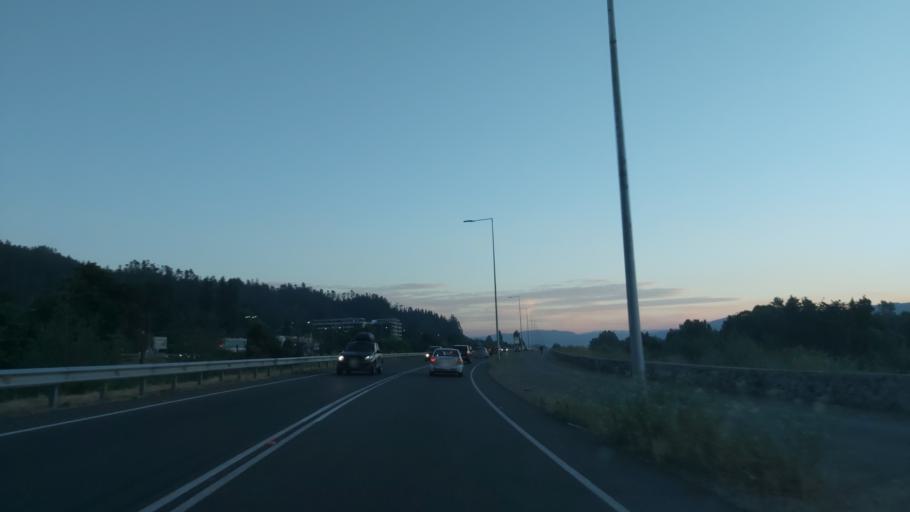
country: CL
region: Biobio
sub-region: Provincia de Concepcion
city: Chiguayante
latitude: -36.8783
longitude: -73.0392
